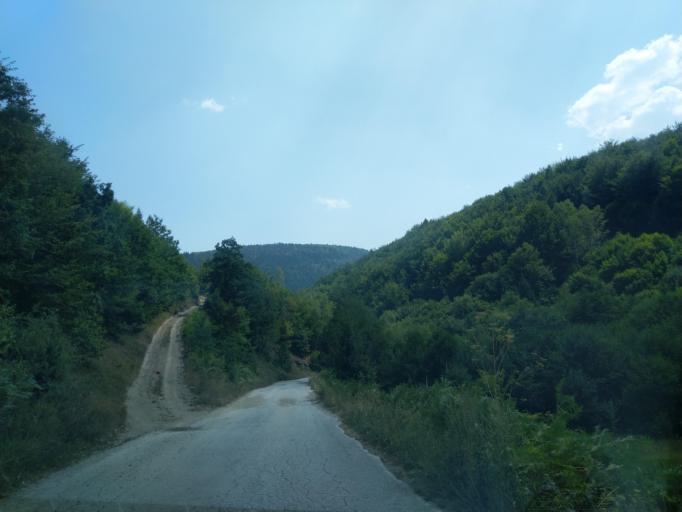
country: RS
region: Central Serbia
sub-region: Zlatiborski Okrug
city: Prijepolje
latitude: 43.3301
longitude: 19.5719
